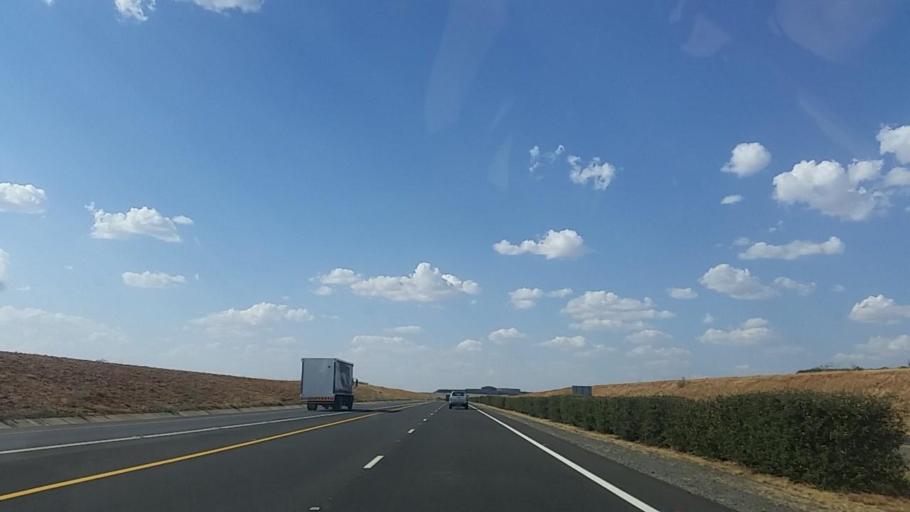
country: ZA
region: Orange Free State
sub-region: Mangaung Metropolitan Municipality
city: Bloemfontein
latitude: -29.1989
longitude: 26.1915
